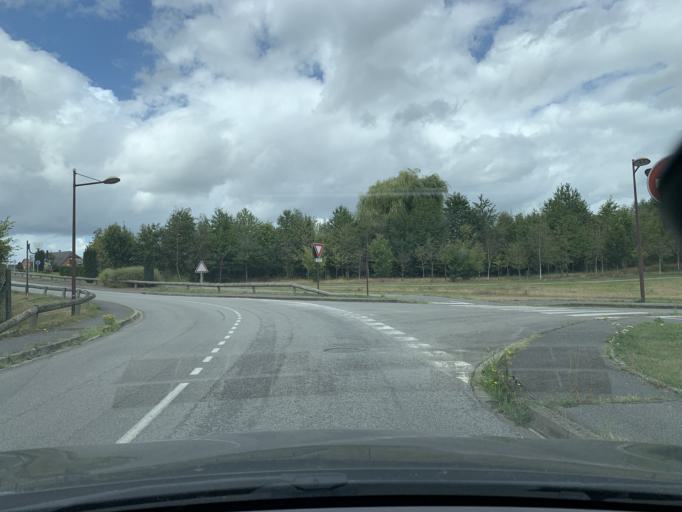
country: FR
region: Picardie
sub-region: Departement de l'Aisne
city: Hirson
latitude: 49.9087
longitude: 4.0702
